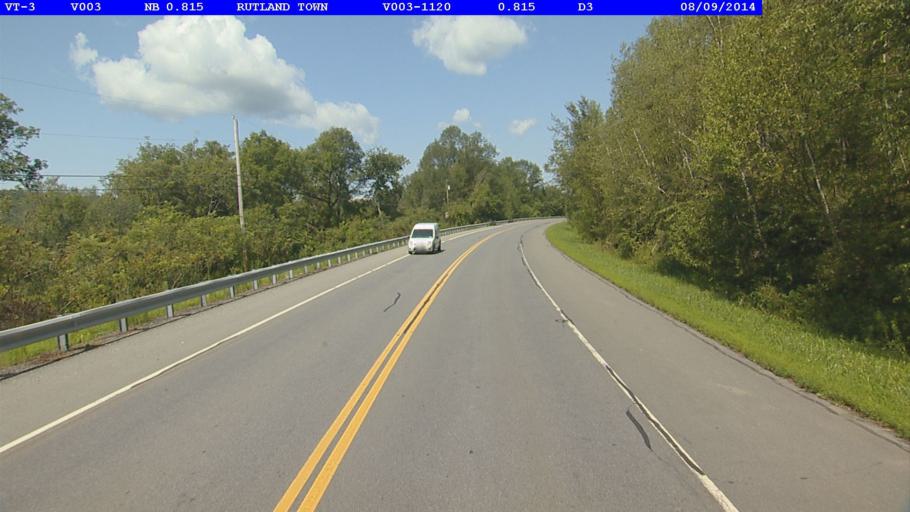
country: US
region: Vermont
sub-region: Rutland County
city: West Rutland
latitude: 43.6149
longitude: -73.0189
